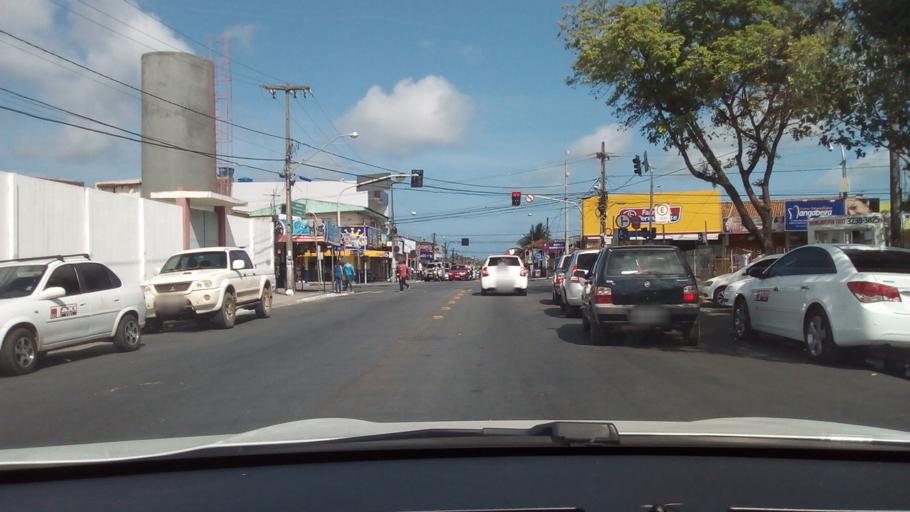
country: BR
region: Paraiba
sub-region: Joao Pessoa
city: Joao Pessoa
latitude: -7.1722
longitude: -34.8401
